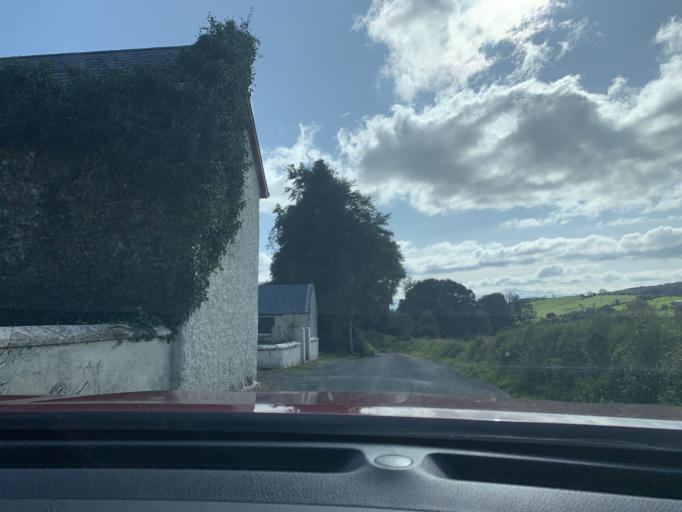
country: IE
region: Connaught
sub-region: Roscommon
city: Boyle
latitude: 54.0771
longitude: -8.3649
